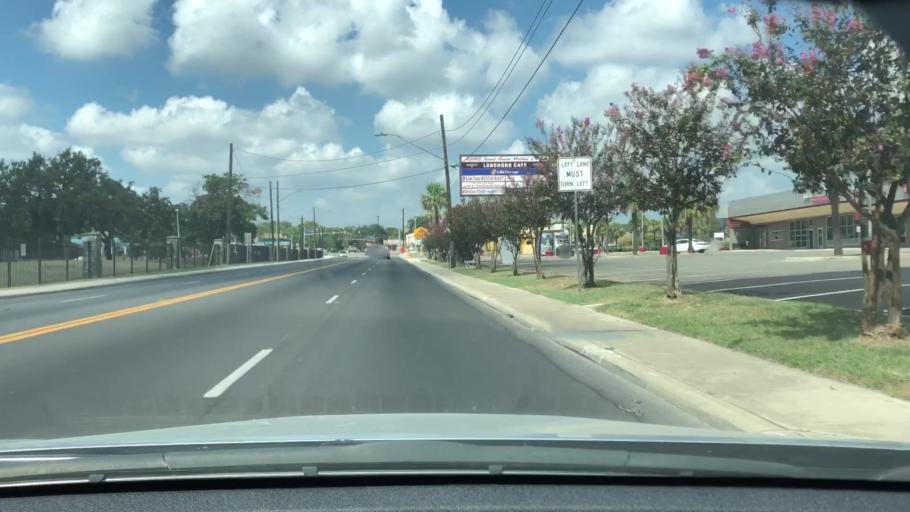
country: US
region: Texas
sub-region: Bexar County
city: Terrell Hills
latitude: 29.4849
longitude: -98.4275
